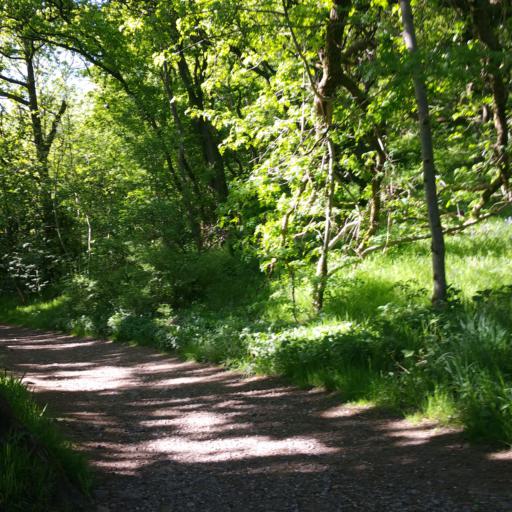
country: GB
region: Scotland
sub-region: East Dunbartonshire
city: Milngavie
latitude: 55.9590
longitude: -4.3318
